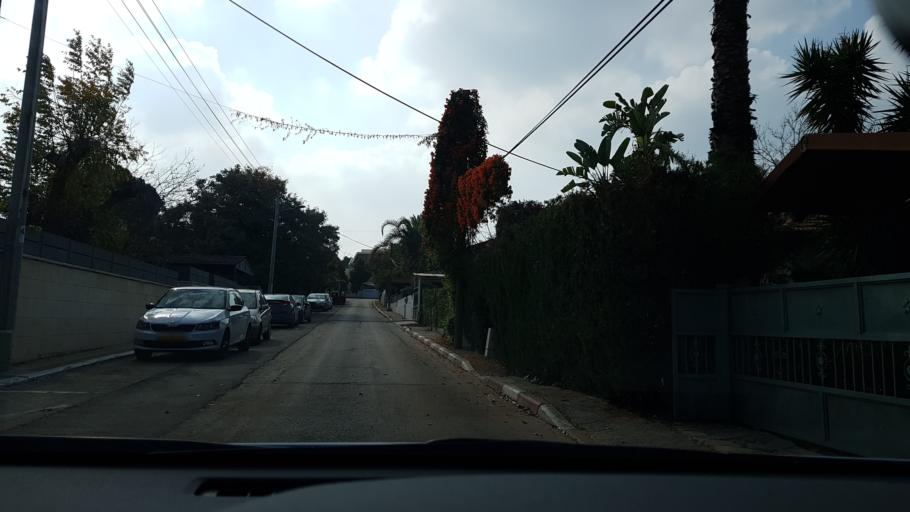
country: IL
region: Central District
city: Mazkeret Batya
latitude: 31.8762
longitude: 34.8126
